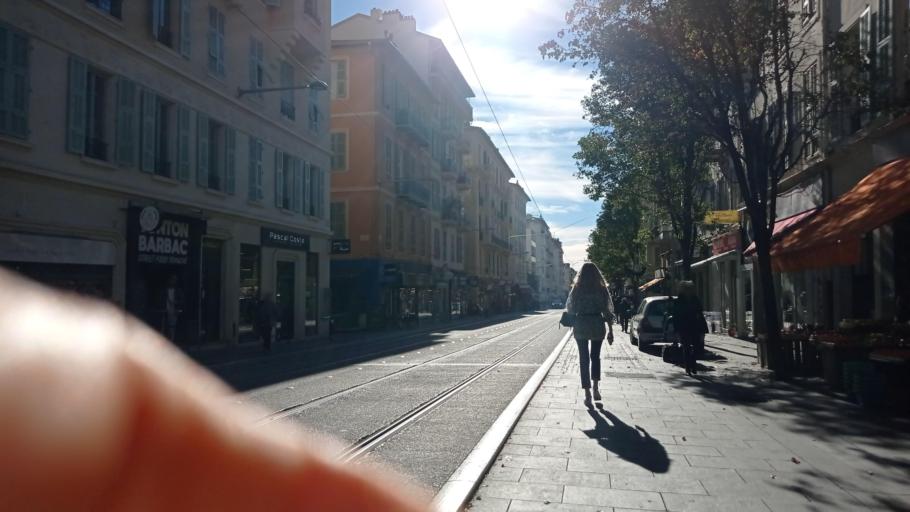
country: FR
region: Provence-Alpes-Cote d'Azur
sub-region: Departement des Alpes-Maritimes
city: Nice
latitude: 43.7146
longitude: 7.2616
